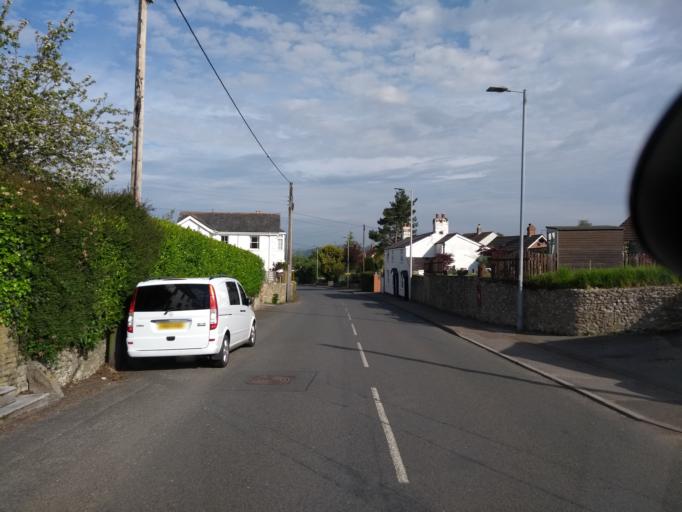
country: GB
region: England
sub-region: Devon
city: Axminster
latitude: 50.7784
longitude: -2.9867
